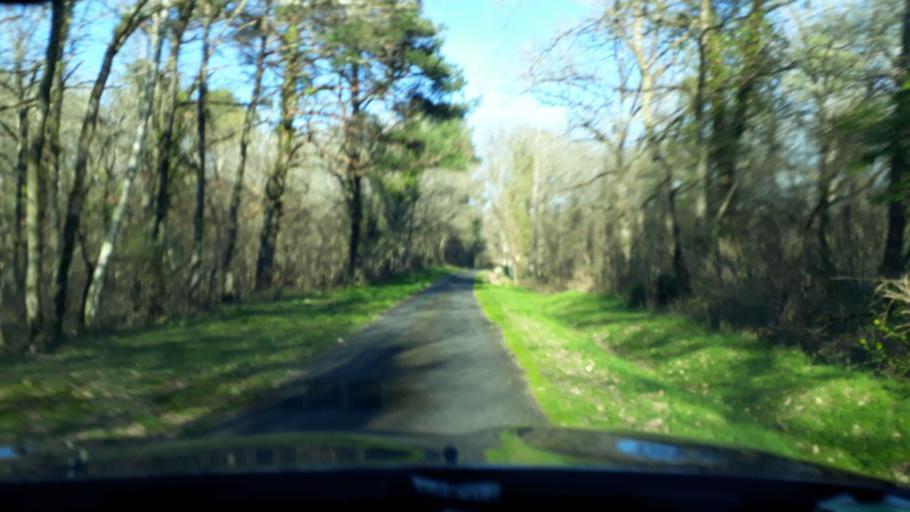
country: FR
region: Centre
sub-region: Departement du Loiret
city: Ligny-le-Ribault
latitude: 47.6923
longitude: 1.7972
